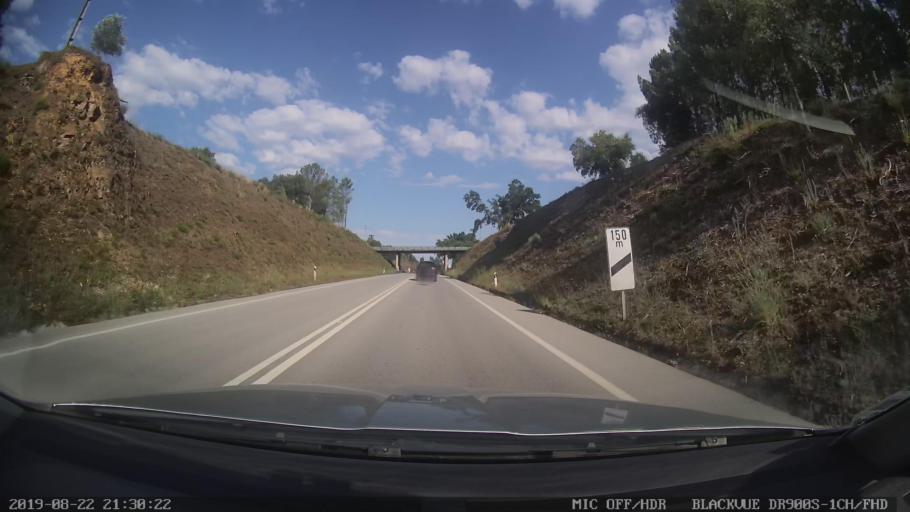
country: PT
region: Leiria
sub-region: Pedrogao Grande
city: Pedrogao Grande
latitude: 39.9093
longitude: -8.1500
